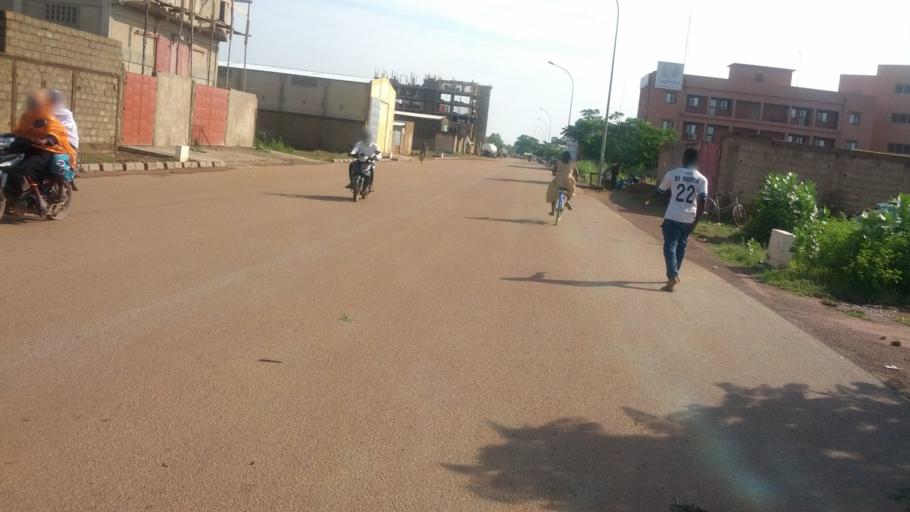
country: BF
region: Centre
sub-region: Kadiogo Province
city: Ouagadougou
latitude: 12.3503
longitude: -1.4934
